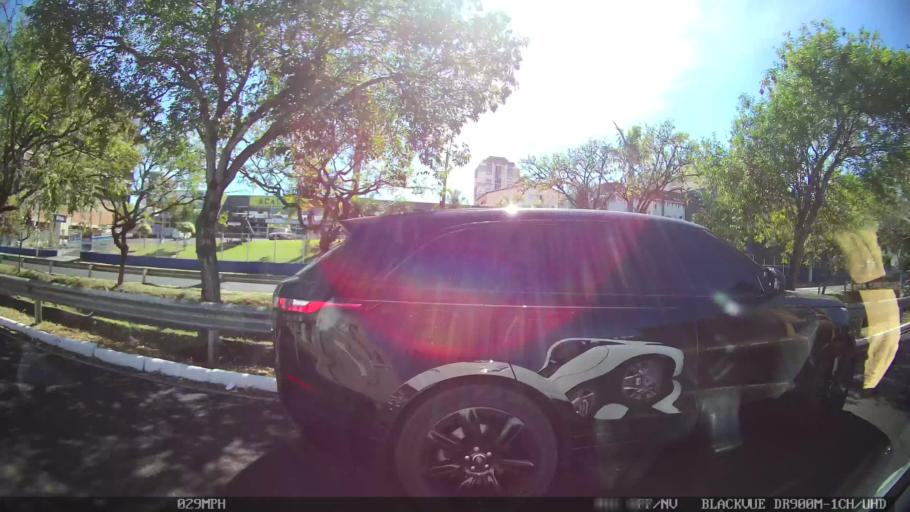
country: BR
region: Sao Paulo
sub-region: Franca
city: Franca
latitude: -20.5374
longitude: -47.3865
